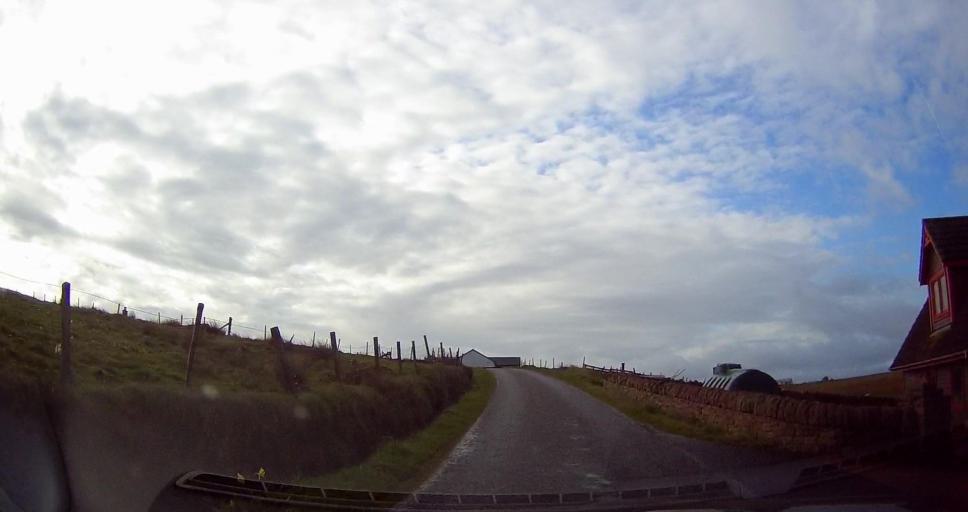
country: GB
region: Scotland
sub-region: Shetland Islands
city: Sandwick
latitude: 60.0444
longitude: -1.2060
